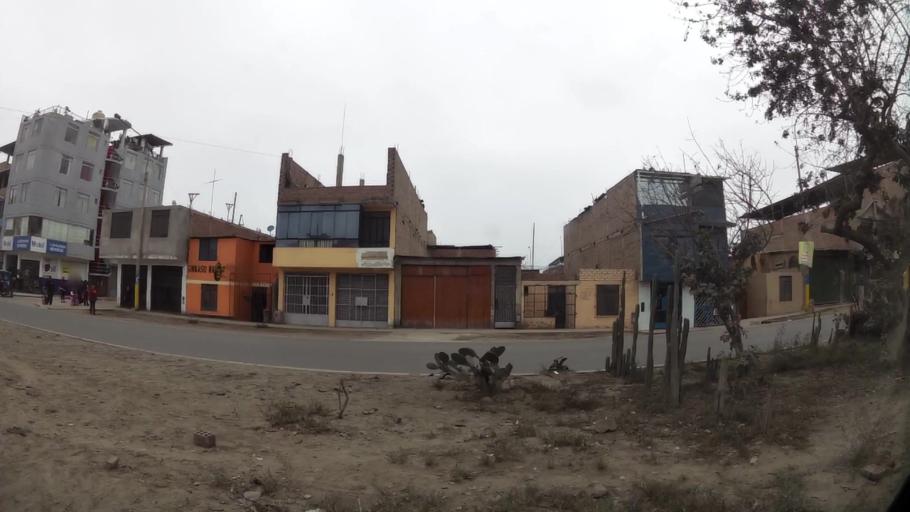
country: PE
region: Lima
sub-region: Lima
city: Surco
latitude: -12.2372
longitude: -76.9224
